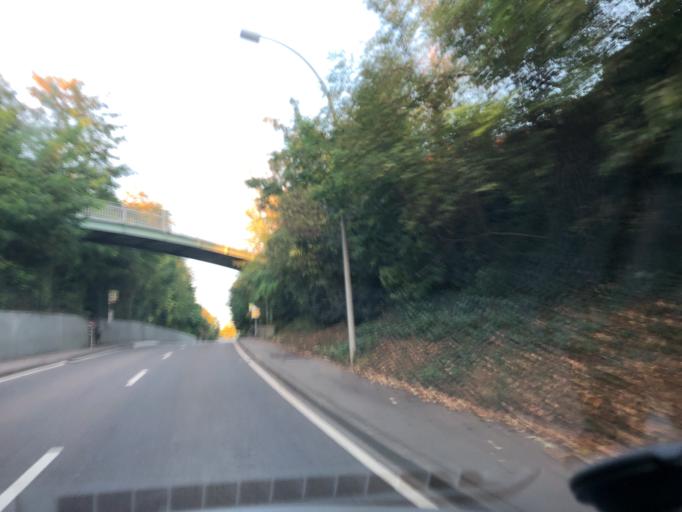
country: DE
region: Baden-Wuerttemberg
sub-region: Regierungsbezirk Stuttgart
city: Freiberg am Neckar
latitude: 48.9115
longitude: 9.2241
